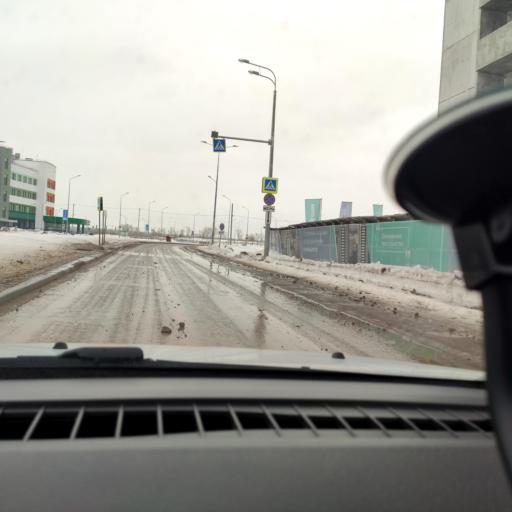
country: RU
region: Samara
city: Samara
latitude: 53.0983
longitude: 50.1738
